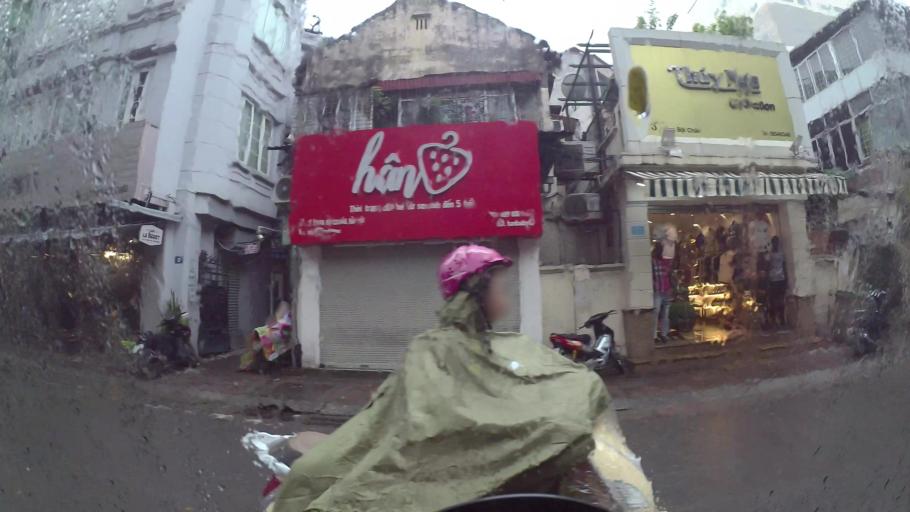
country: VN
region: Ha Noi
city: Hanoi
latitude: 21.0275
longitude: 105.8439
